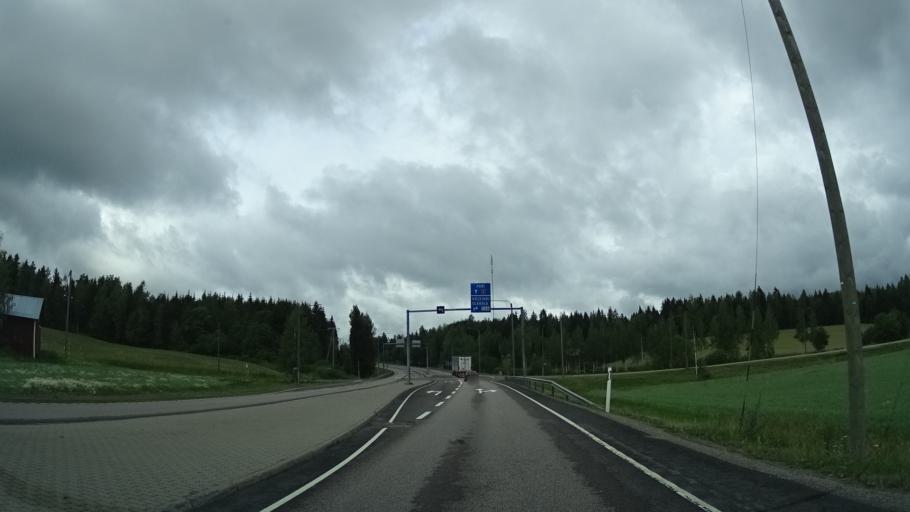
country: FI
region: Uusimaa
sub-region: Helsinki
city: Vihti
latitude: 60.4619
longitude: 24.3173
